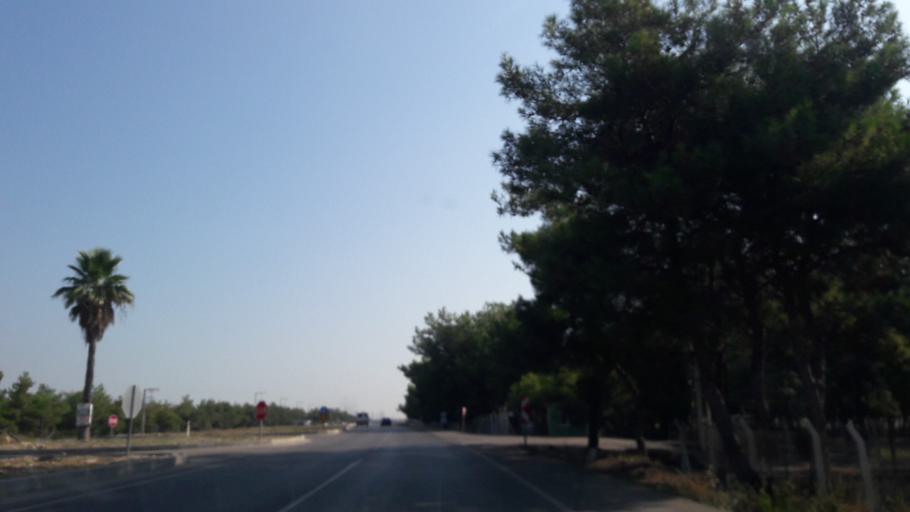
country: TR
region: Adana
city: Yakapinar
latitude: 37.0903
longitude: 35.4924
